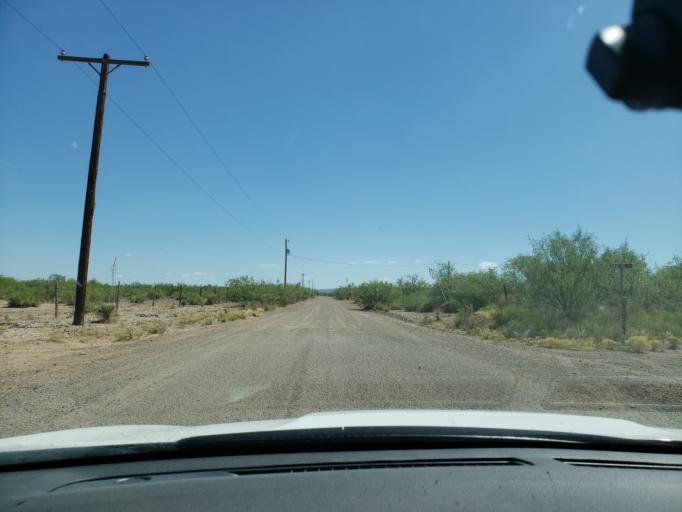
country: US
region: Texas
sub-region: Presidio County
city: Marfa
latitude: 30.5921
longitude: -104.4915
